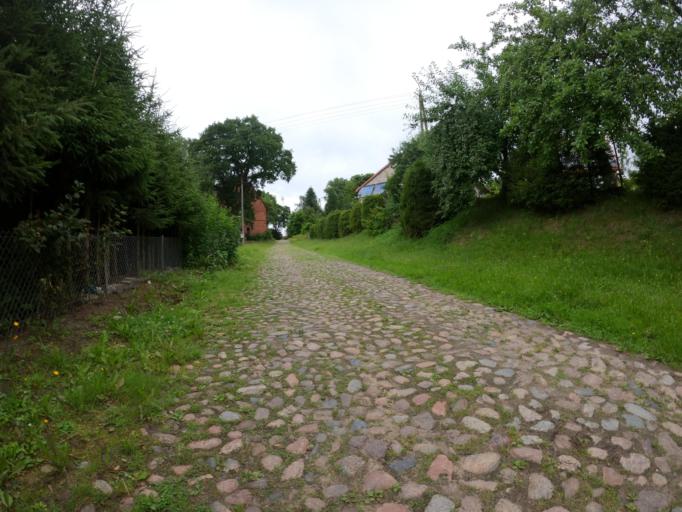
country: PL
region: West Pomeranian Voivodeship
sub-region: Powiat koszalinski
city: Bobolice
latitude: 53.9250
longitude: 16.4920
